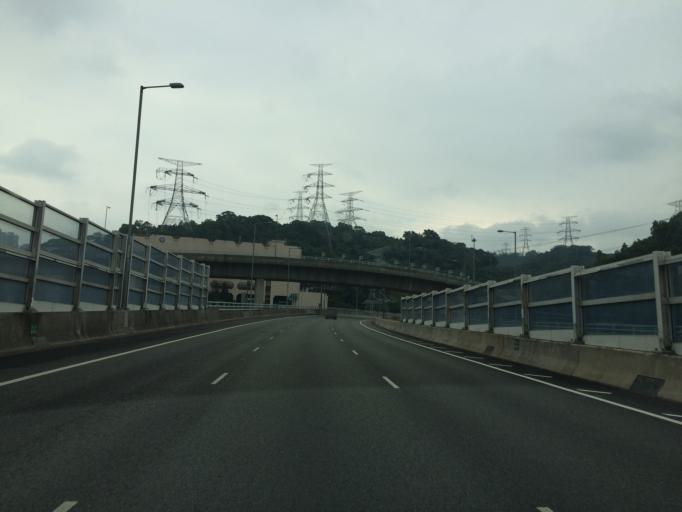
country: HK
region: Sham Shui Po
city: Sham Shui Po
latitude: 22.3394
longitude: 114.1440
